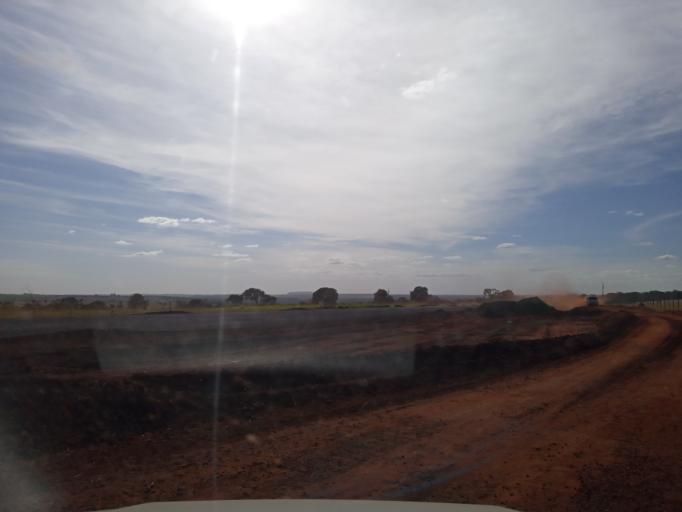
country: BR
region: Minas Gerais
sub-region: Ituiutaba
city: Ituiutaba
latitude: -18.9714
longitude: -49.5054
